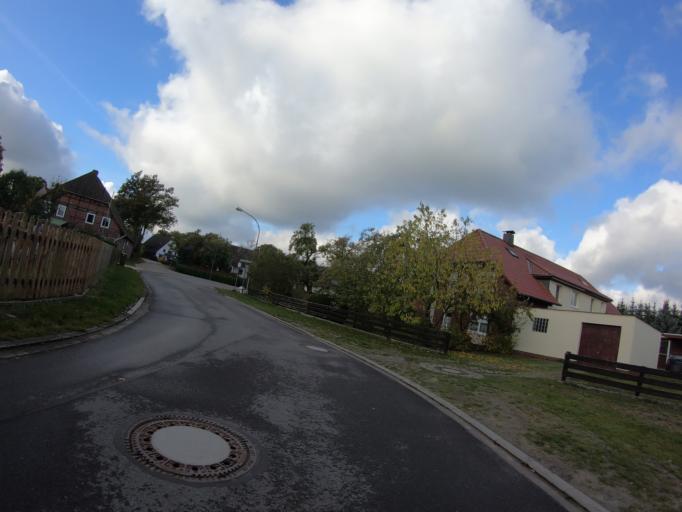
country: DE
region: Lower Saxony
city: Wagenhoff
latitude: 52.5207
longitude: 10.5402
